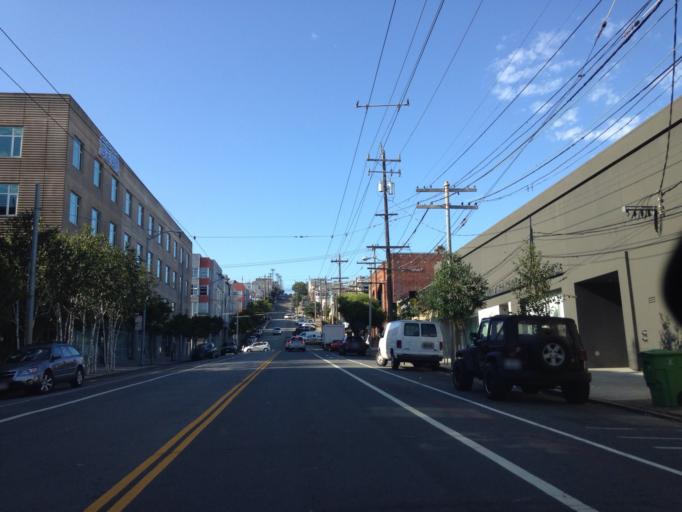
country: US
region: California
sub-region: San Francisco County
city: San Francisco
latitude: 37.7657
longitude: -122.4036
